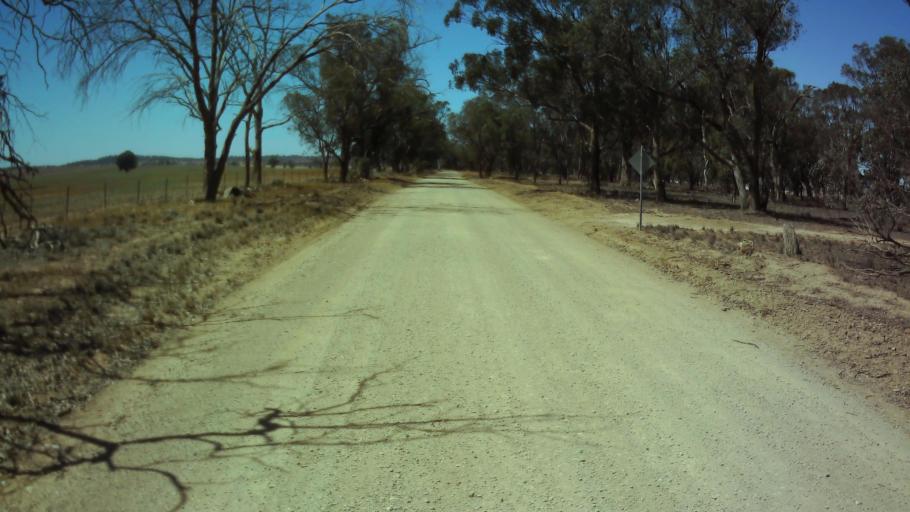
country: AU
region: New South Wales
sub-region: Weddin
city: Grenfell
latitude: -33.8747
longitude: 148.0887
